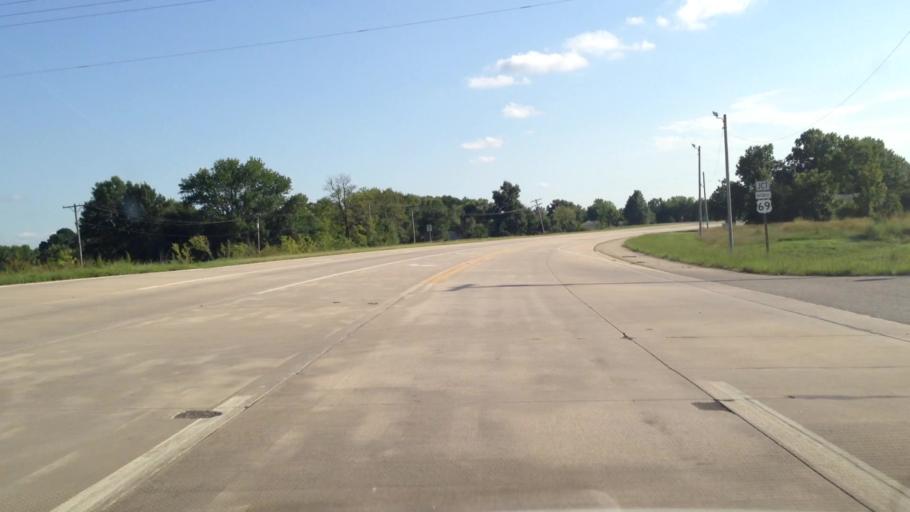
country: US
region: Kansas
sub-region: Crawford County
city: Arma
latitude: 37.5580
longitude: -94.7046
